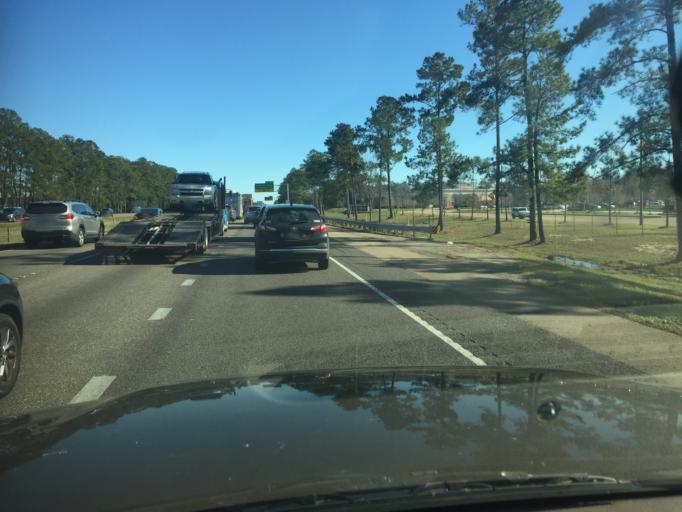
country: US
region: Louisiana
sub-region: Saint Tammany Parish
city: Covington
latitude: 30.4449
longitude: -90.1347
